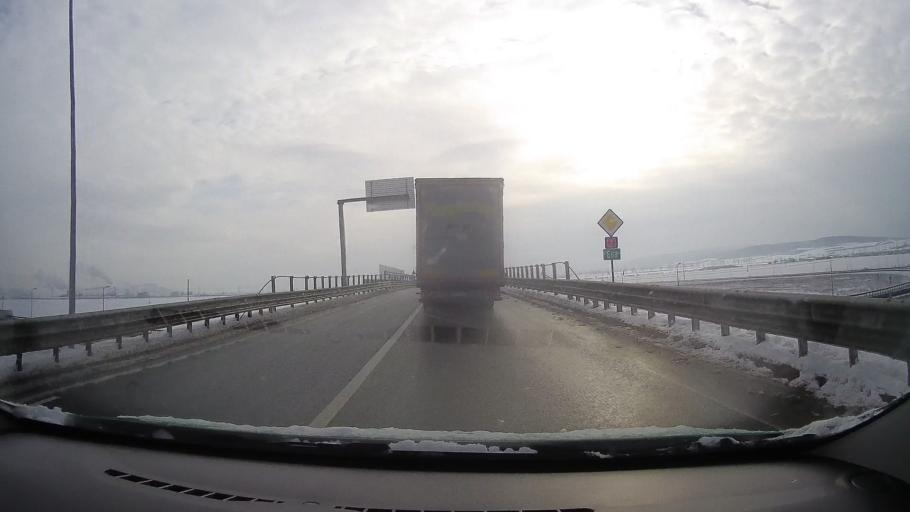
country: RO
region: Alba
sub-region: Municipiul Sebes
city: Lancram
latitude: 45.9777
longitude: 23.5211
